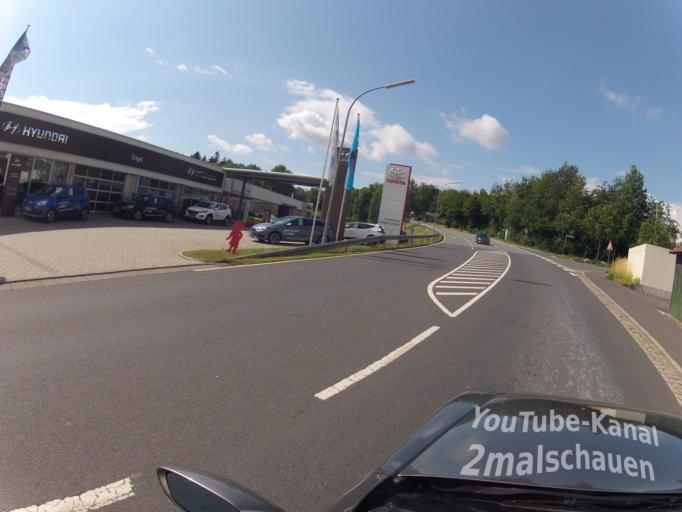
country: DE
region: Bavaria
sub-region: Upper Franconia
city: Wunsiedel
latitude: 50.0433
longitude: 11.9956
